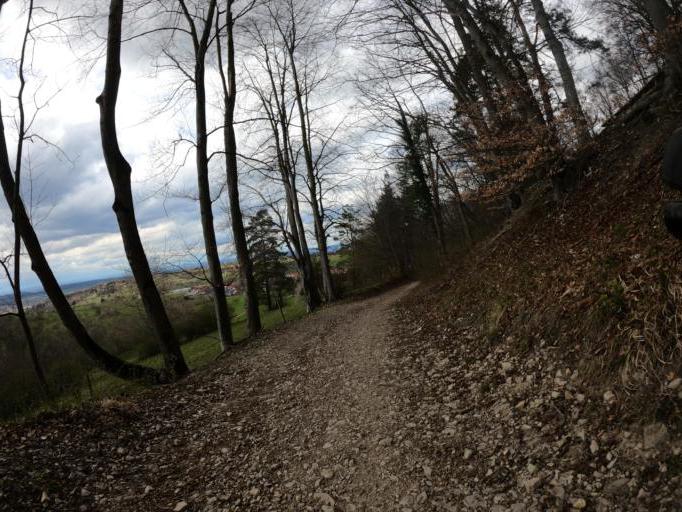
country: DE
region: Baden-Wuerttemberg
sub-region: Tuebingen Region
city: Gomaringen
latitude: 48.4058
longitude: 9.1154
